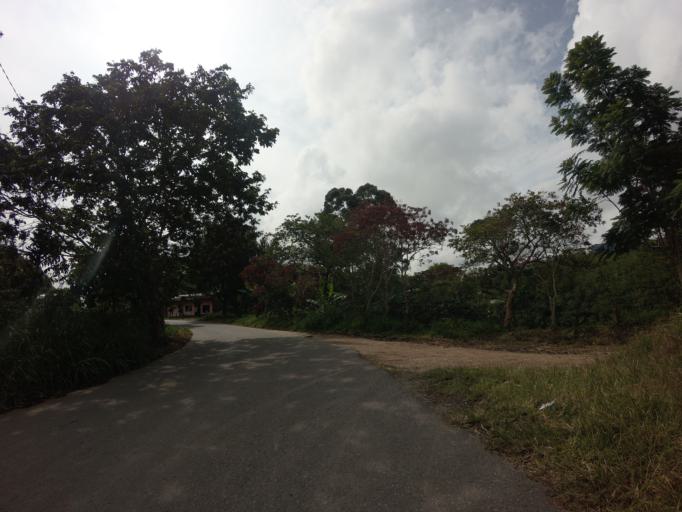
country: CO
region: Caldas
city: Marquetalia
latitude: 5.2983
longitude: -75.0443
